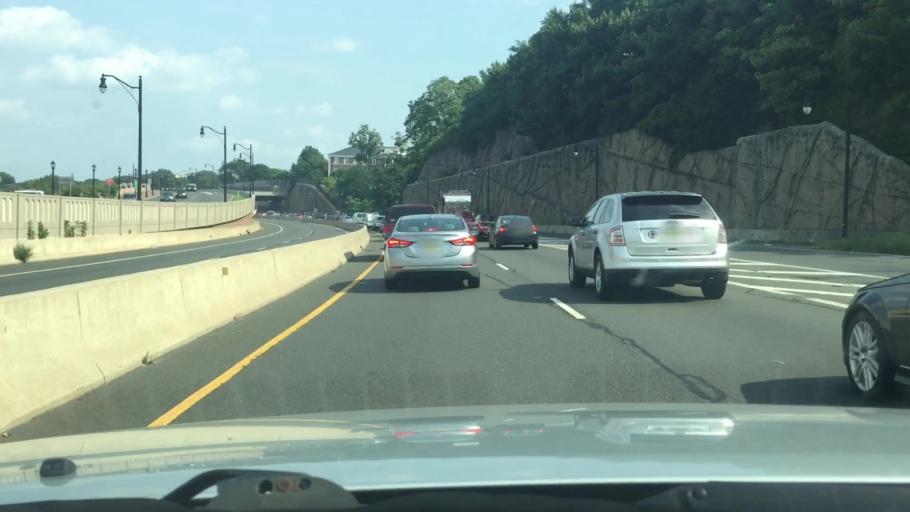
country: US
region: New Jersey
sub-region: Middlesex County
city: Highland Park
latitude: 40.4884
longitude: -74.4359
